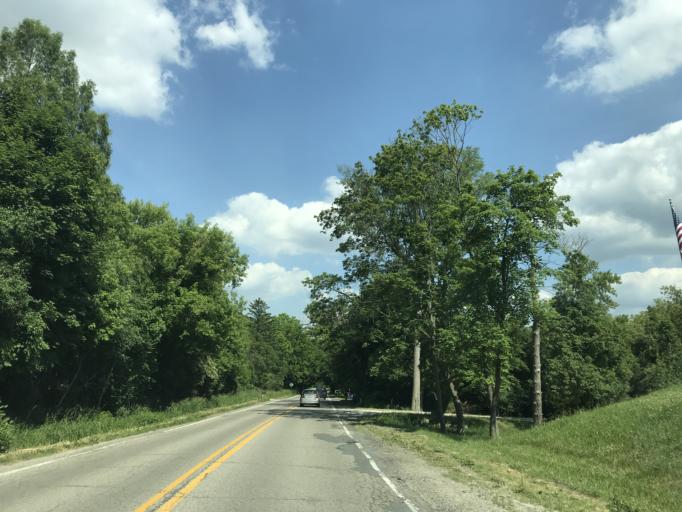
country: US
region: Michigan
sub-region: Washtenaw County
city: Ypsilanti
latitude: 42.2793
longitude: -83.6459
